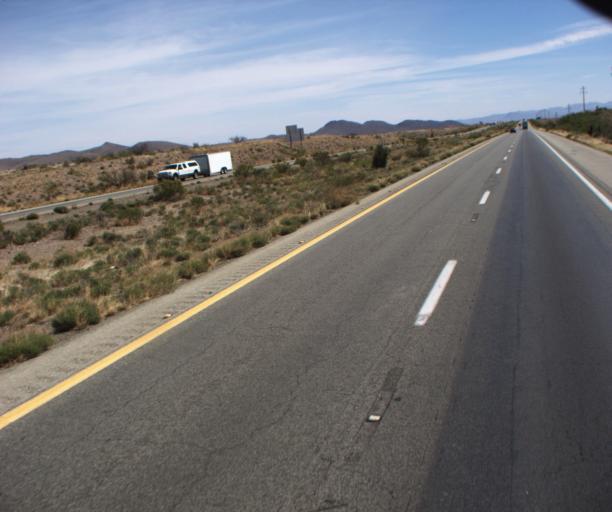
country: US
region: Arizona
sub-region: Cochise County
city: Willcox
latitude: 32.3604
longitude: -109.6663
